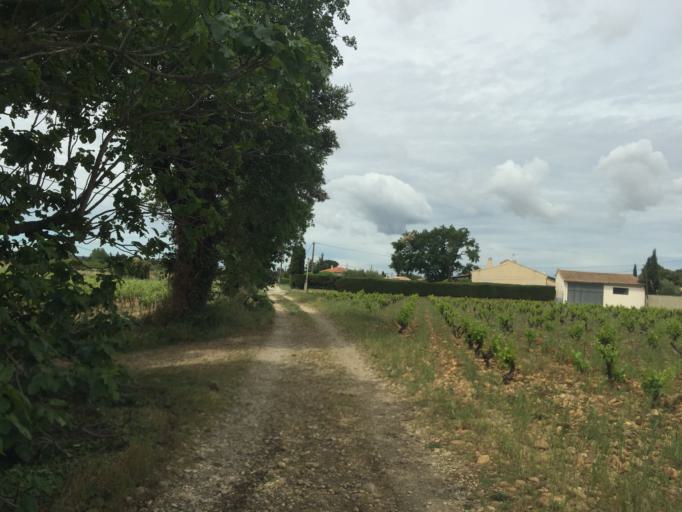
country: FR
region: Provence-Alpes-Cote d'Azur
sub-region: Departement du Vaucluse
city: Sorgues
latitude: 44.0332
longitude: 4.8729
